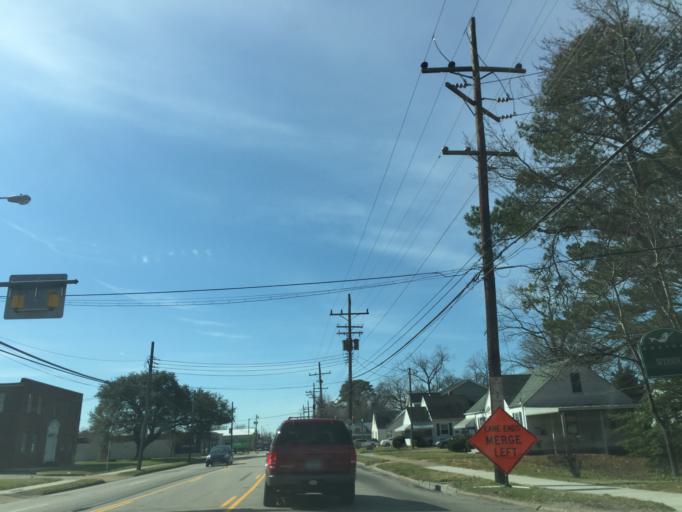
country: US
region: Virginia
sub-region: City of Norfolk
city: Norfolk
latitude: 36.8806
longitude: -76.2625
